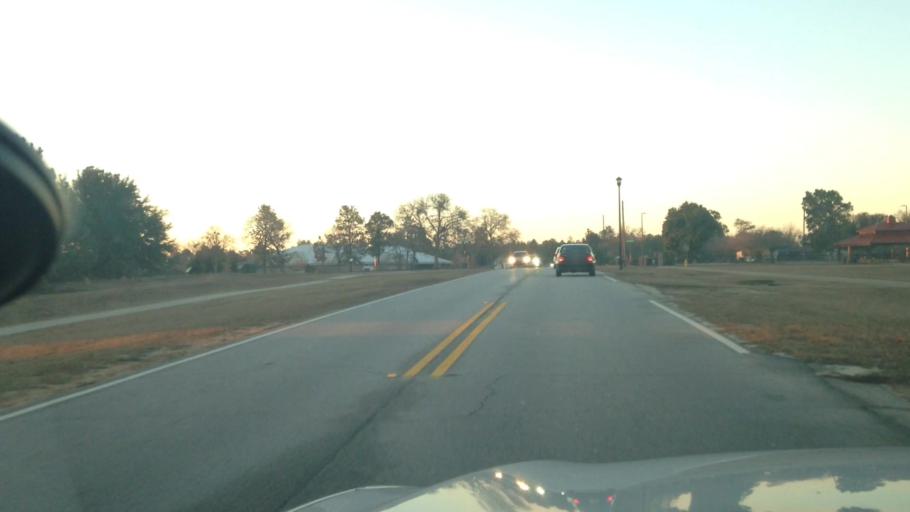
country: US
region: Georgia
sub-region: Columbia County
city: Grovetown
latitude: 33.4222
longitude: -82.1354
